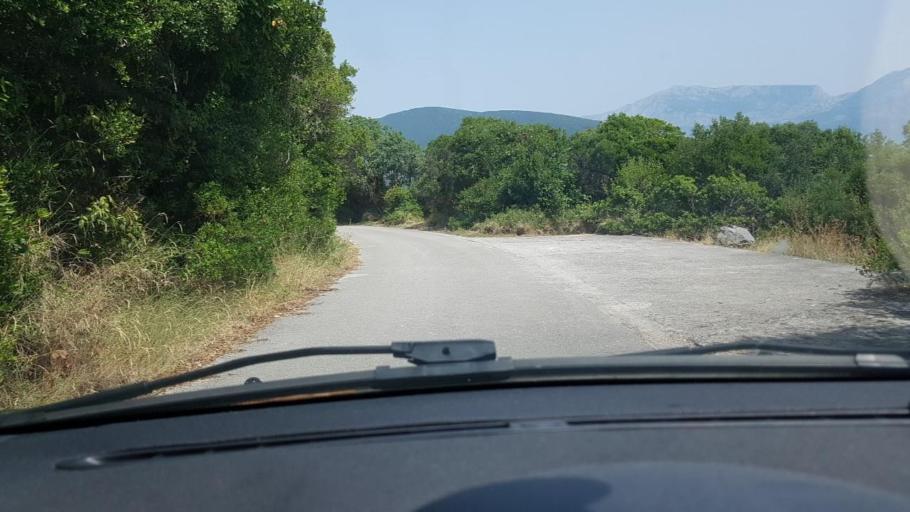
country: ME
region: Herceg Novi
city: Herceg-Novi
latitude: 42.3993
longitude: 18.5211
